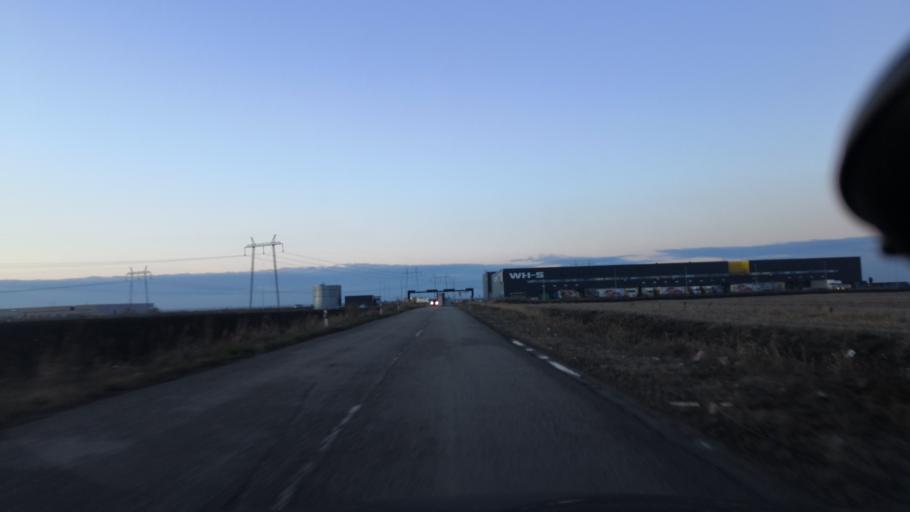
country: RS
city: Simanovci
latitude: 44.8895
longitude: 20.1099
